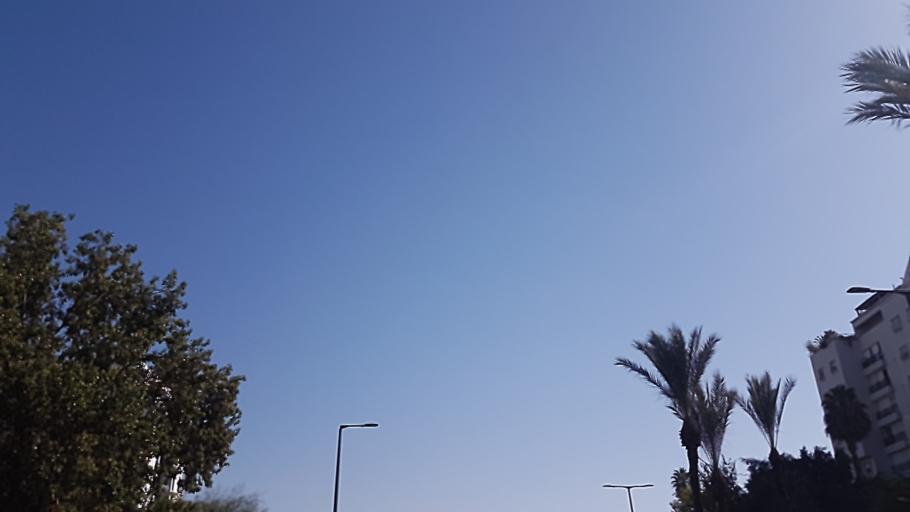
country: IL
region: Tel Aviv
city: Giv`atayim
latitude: 32.0610
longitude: 34.8209
